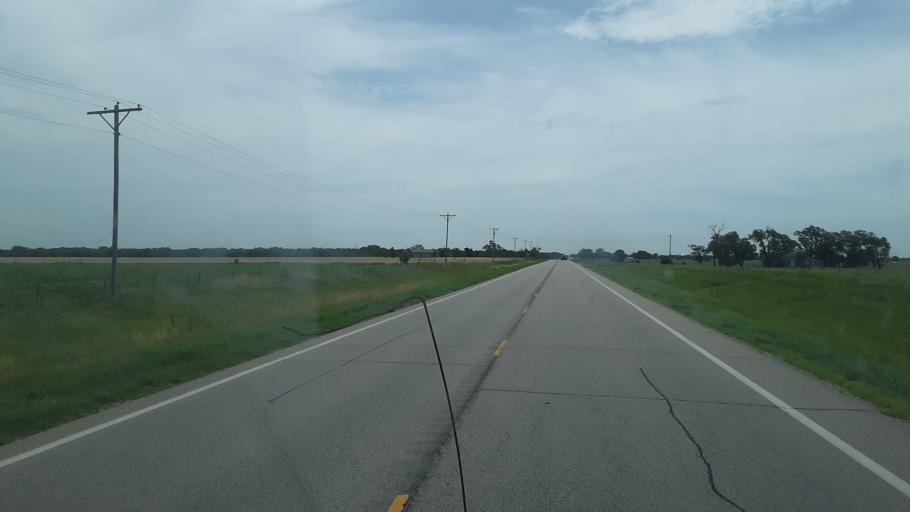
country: US
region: Kansas
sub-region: Butler County
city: El Dorado
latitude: 37.8106
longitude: -96.6428
